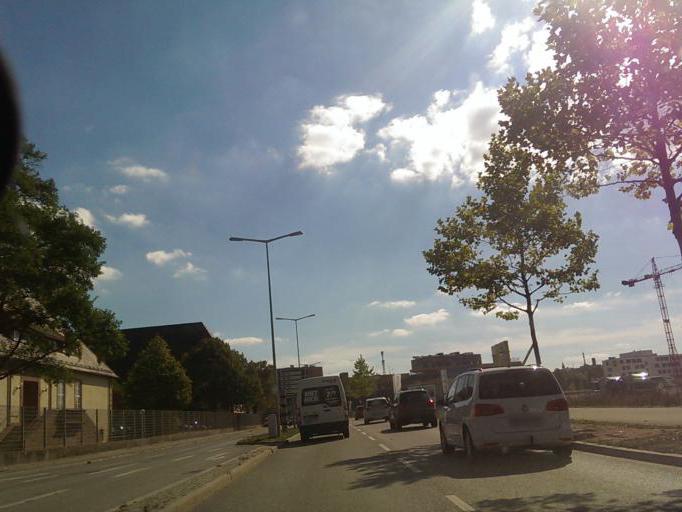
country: DE
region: Baden-Wuerttemberg
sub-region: Regierungsbezirk Stuttgart
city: Boeblingen
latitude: 48.6917
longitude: 9.0049
